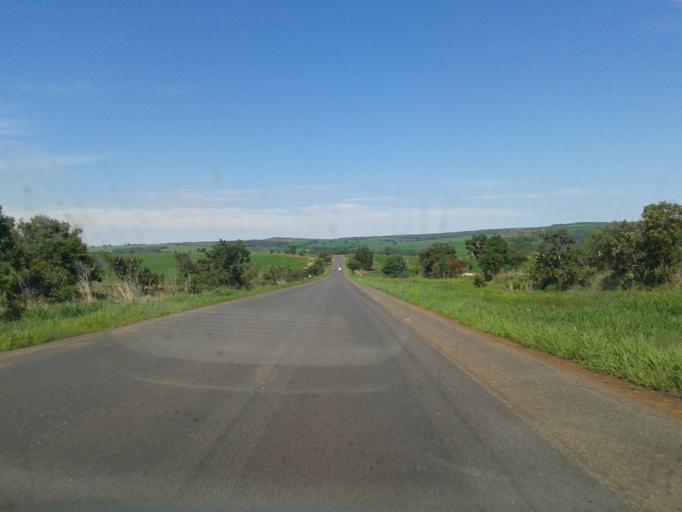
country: BR
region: Goias
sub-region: Bela Vista De Goias
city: Bela Vista de Goias
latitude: -17.1693
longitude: -48.7547
